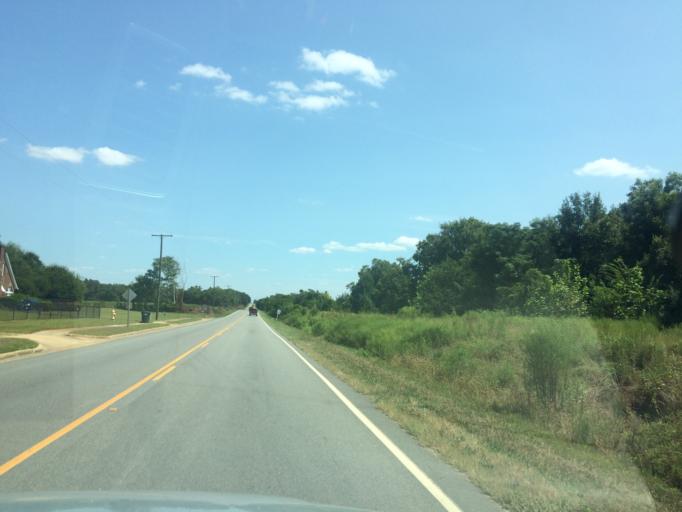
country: US
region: South Carolina
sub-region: Aiken County
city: Aiken
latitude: 33.5267
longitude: -81.6310
